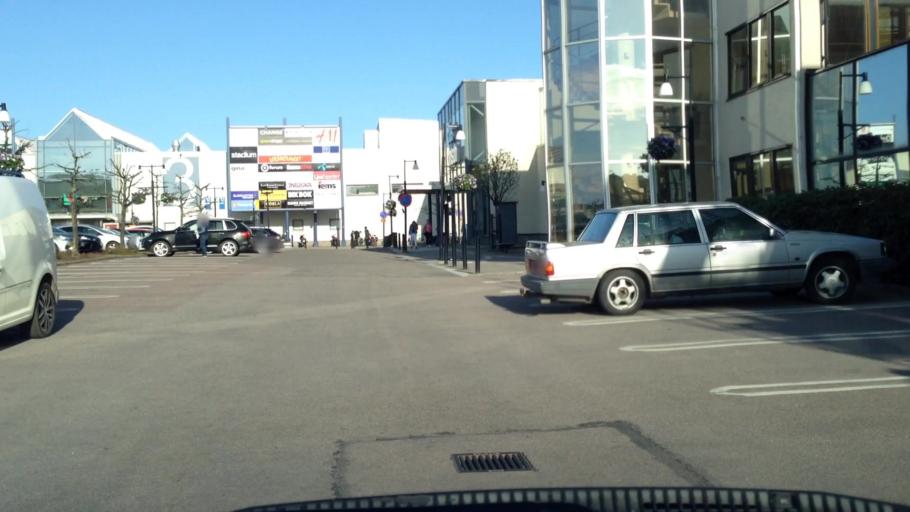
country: SE
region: Halland
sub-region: Kungsbacka Kommun
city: Kungsbacka
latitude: 57.4920
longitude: 12.0725
